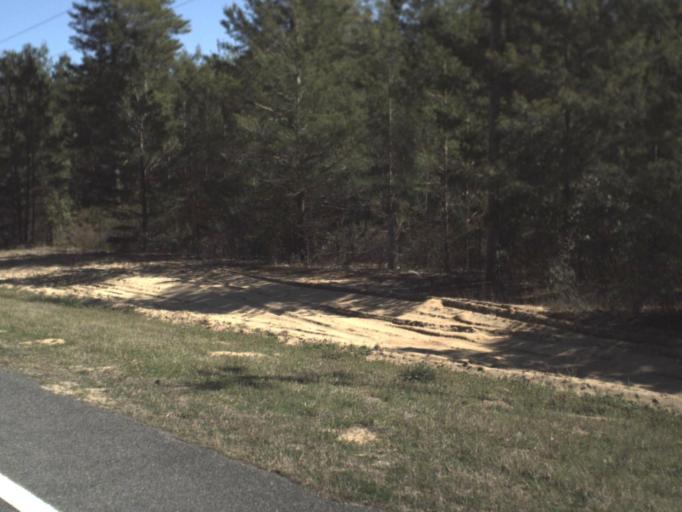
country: US
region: Florida
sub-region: Bay County
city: Lynn Haven
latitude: 30.4257
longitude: -85.6309
